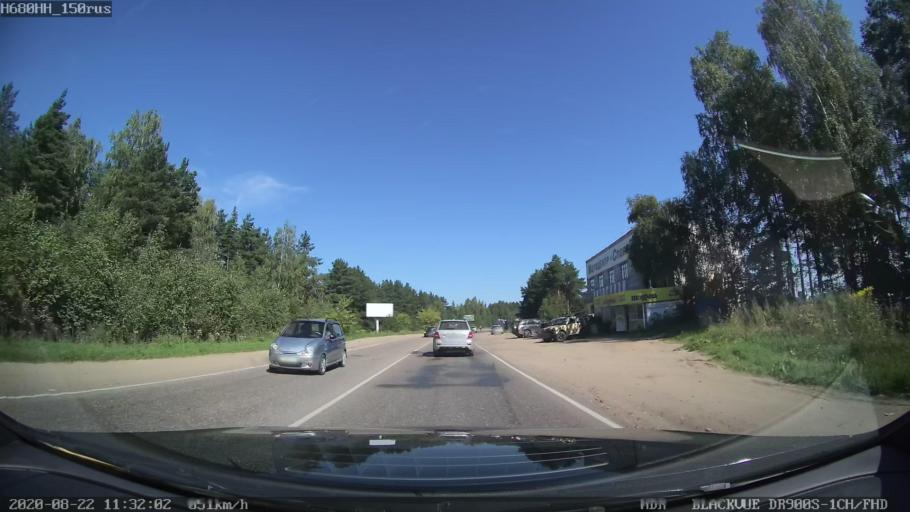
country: RU
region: Tverskaya
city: Tver
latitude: 56.9047
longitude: 35.9333
